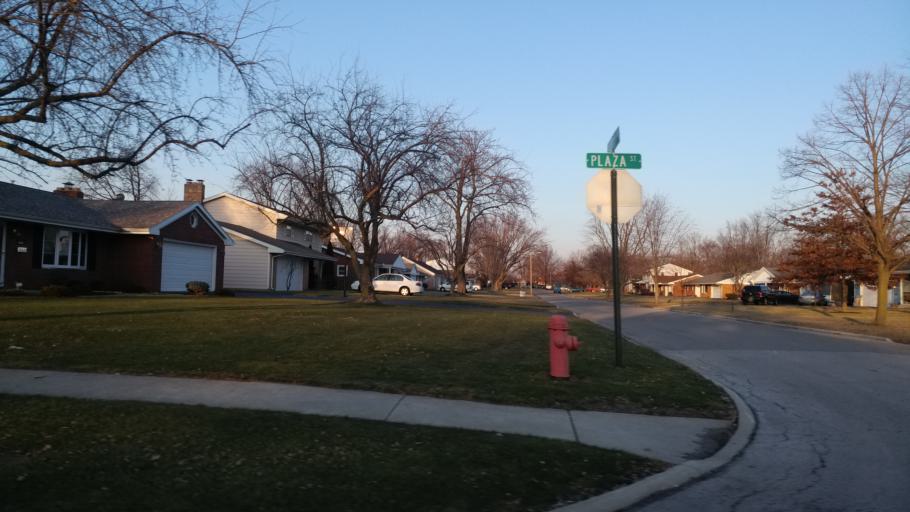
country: US
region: Ohio
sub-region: Hancock County
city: Findlay
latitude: 41.0563
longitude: -83.6184
